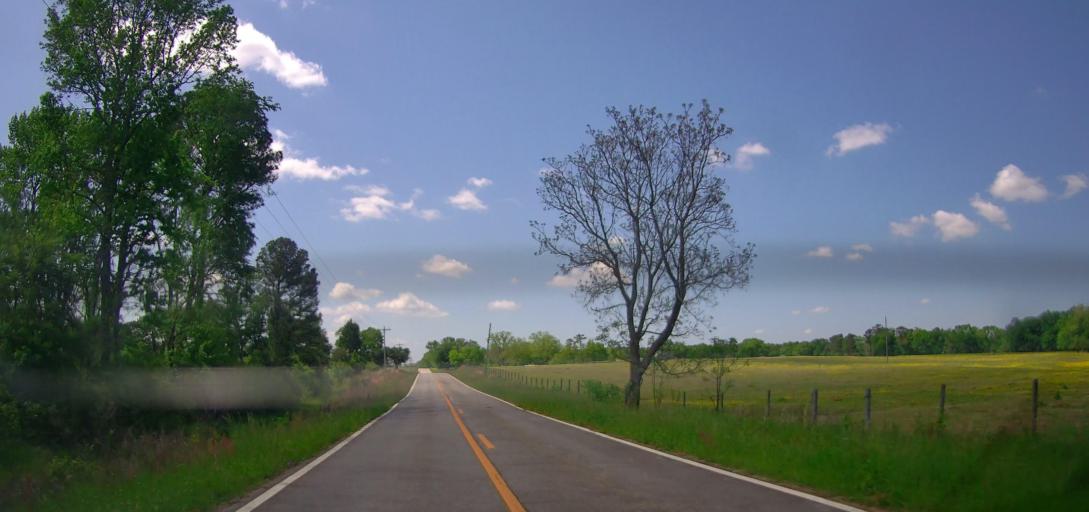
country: US
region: Georgia
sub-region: Putnam County
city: Eatonton
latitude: 33.3286
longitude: -83.3157
